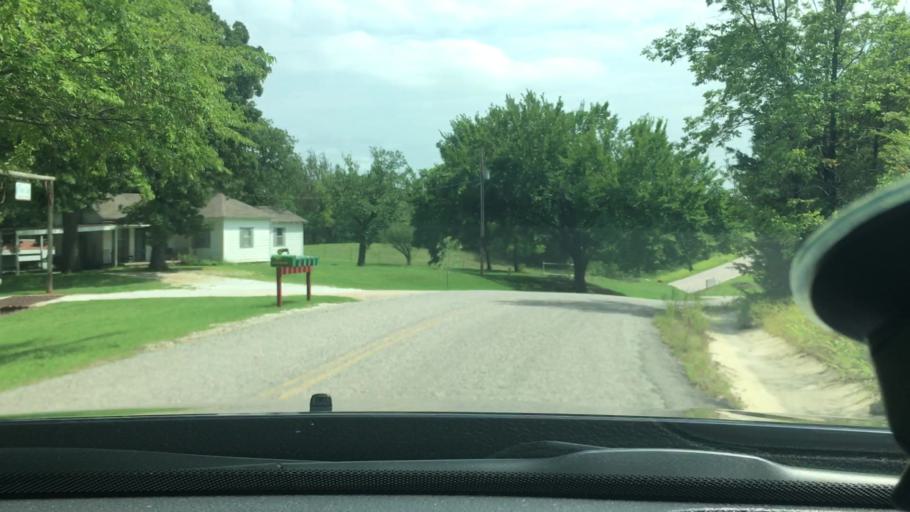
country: US
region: Oklahoma
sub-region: Pontotoc County
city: Ada
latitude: 34.8121
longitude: -96.7096
